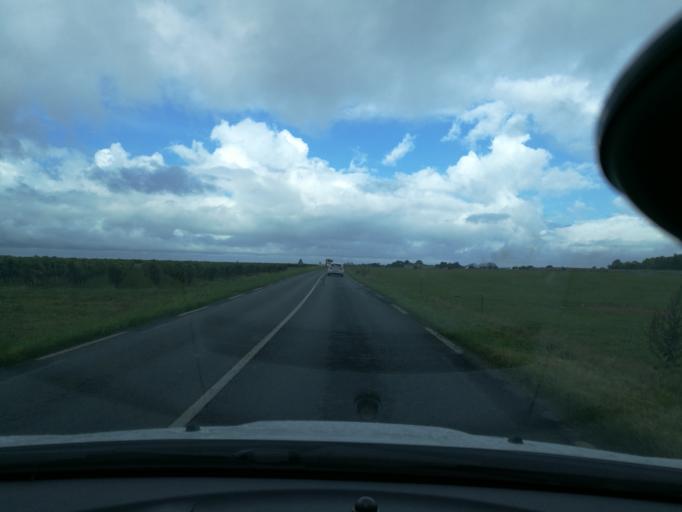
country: FR
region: Poitou-Charentes
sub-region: Departement de la Charente-Maritime
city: Saint-Martin-de-Re
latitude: 46.1976
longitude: -1.3666
